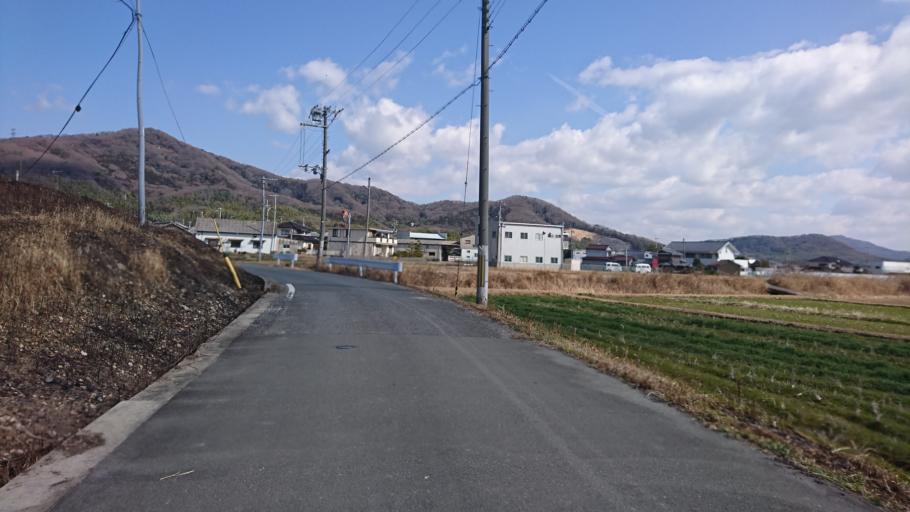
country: JP
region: Hyogo
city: Kakogawacho-honmachi
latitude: 34.8227
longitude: 134.8027
